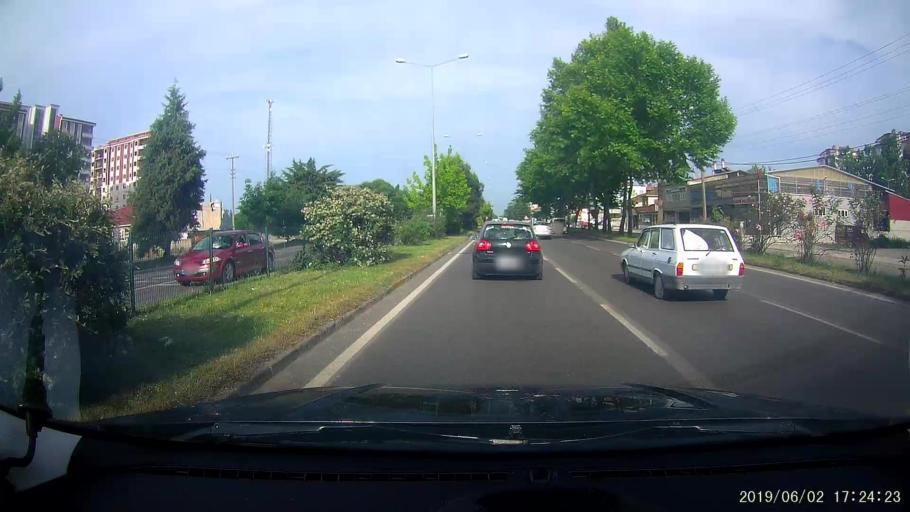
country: TR
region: Samsun
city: Carsamba
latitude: 41.2056
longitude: 36.7009
